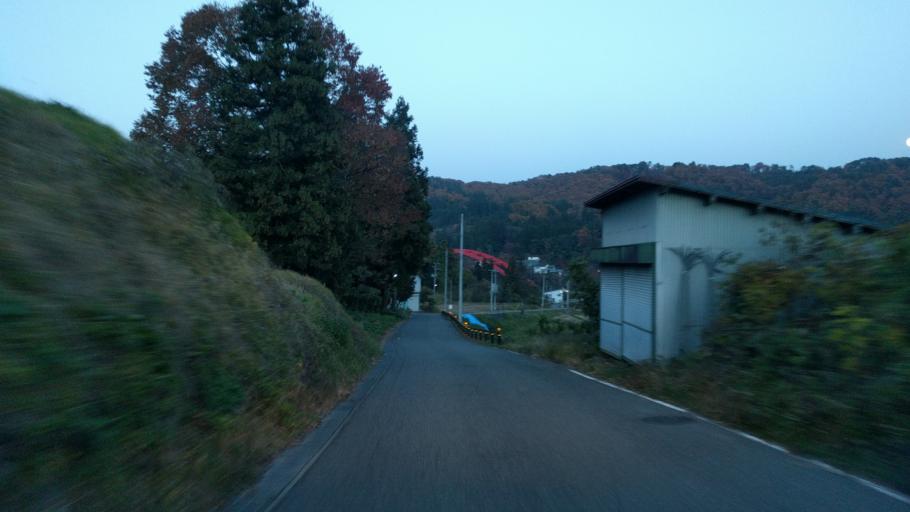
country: JP
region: Fukushima
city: Kitakata
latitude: 37.5311
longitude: 139.7178
